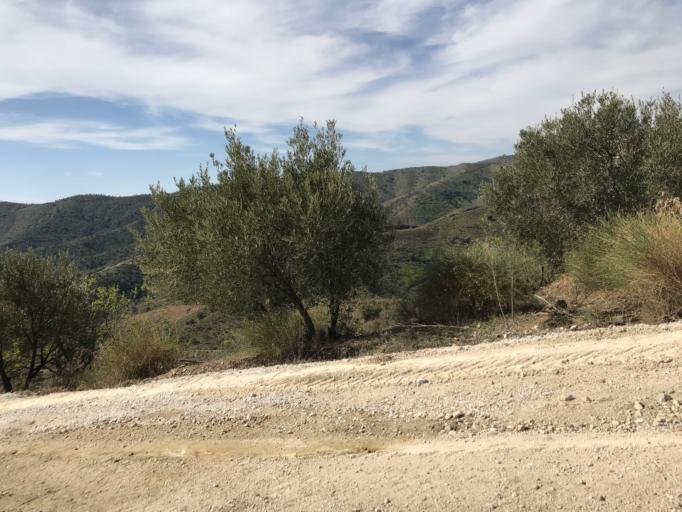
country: ES
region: Andalusia
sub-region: Provincia de Malaga
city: Valdes
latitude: 36.7754
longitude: -4.2176
